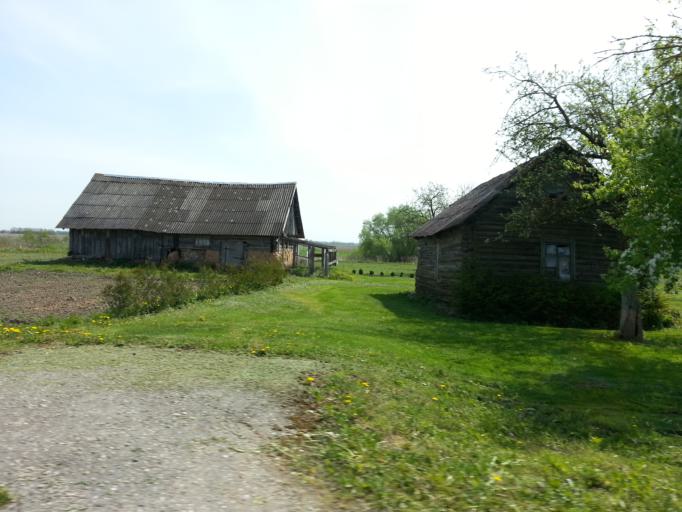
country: LT
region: Panevezys
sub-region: Panevezys City
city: Panevezys
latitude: 55.8859
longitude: 24.2331
